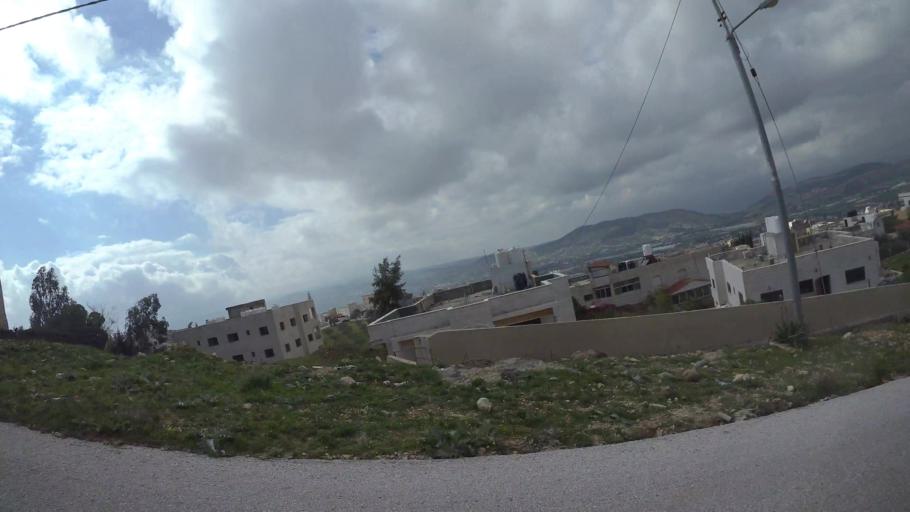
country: JO
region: Amman
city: Al Jubayhah
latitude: 32.0726
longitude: 35.8694
